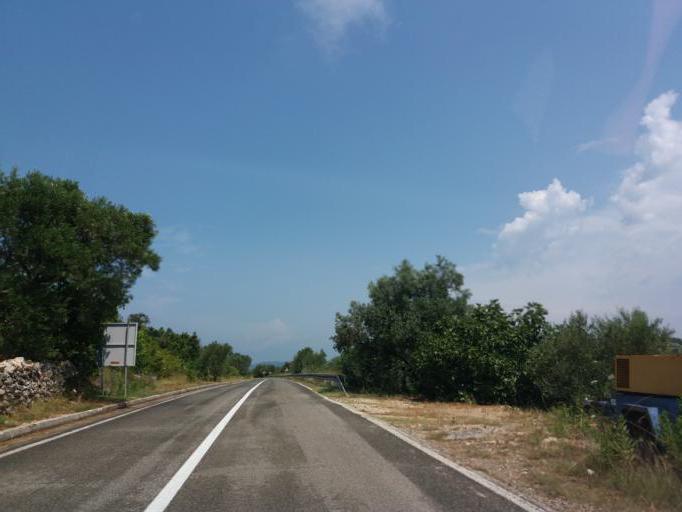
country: HR
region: Zadarska
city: Sali
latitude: 43.9482
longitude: 15.1374
